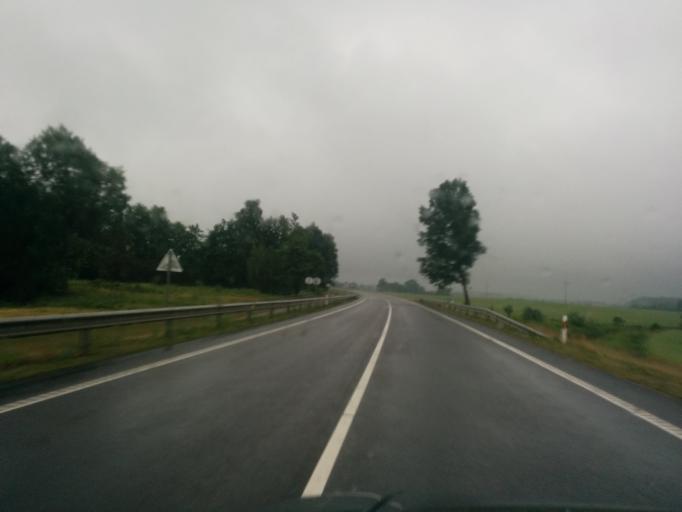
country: LT
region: Panevezys
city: Pasvalys
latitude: 56.1821
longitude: 24.4358
